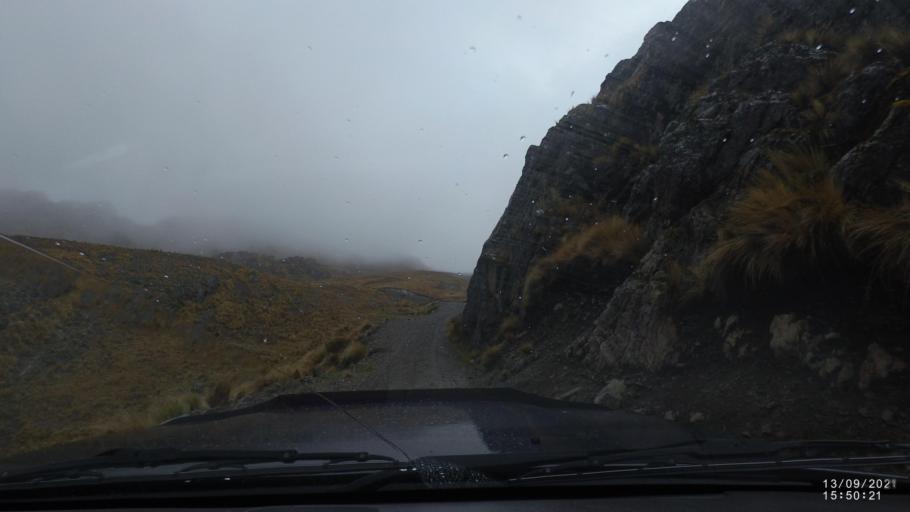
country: BO
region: Cochabamba
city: Colomi
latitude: -17.3059
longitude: -65.7156
